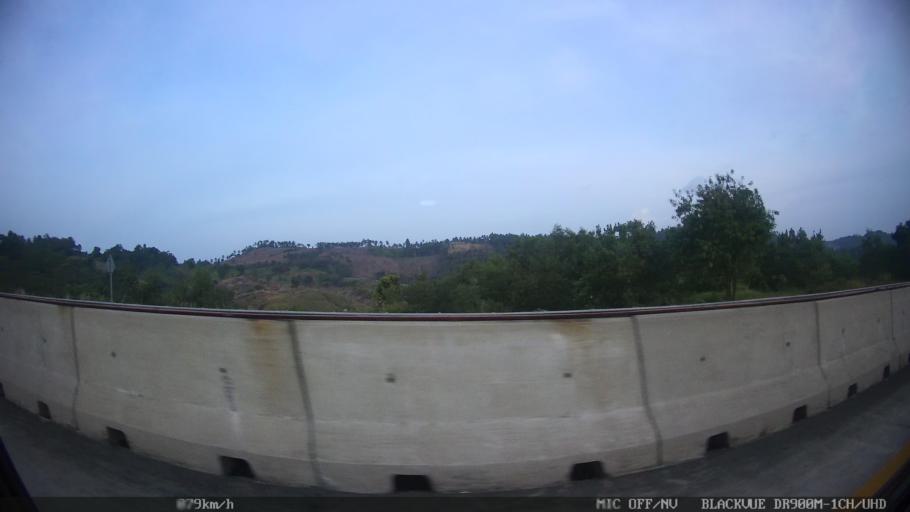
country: ID
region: Lampung
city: Penengahan
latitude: -5.8332
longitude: 105.7315
